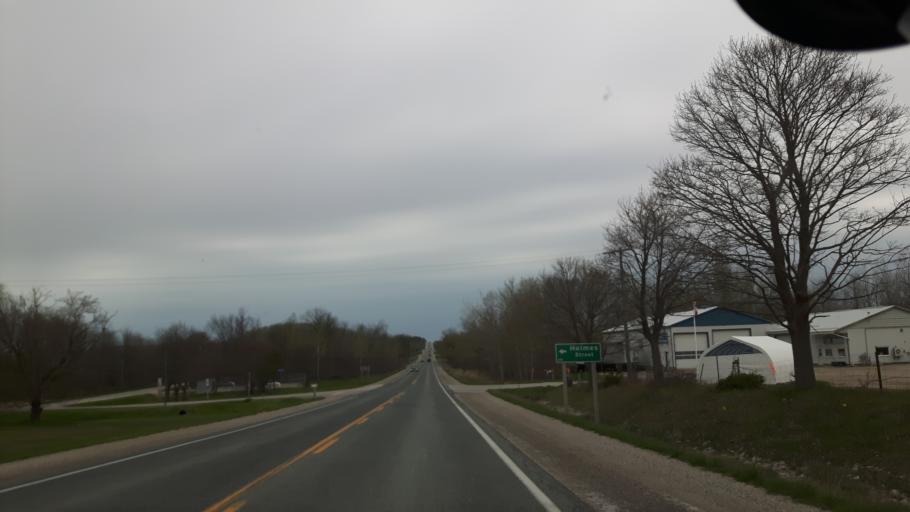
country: CA
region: Ontario
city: Goderich
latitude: 43.6393
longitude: -81.5899
